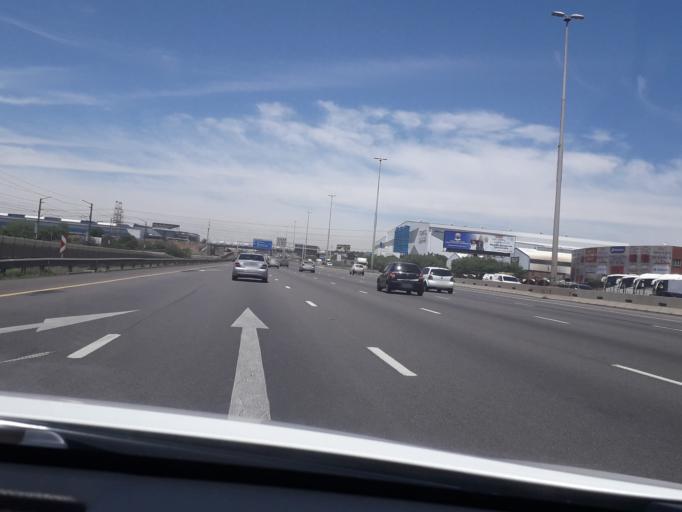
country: ZA
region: Gauteng
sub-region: City of Tshwane Metropolitan Municipality
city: Centurion
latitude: -25.8861
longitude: 28.1668
